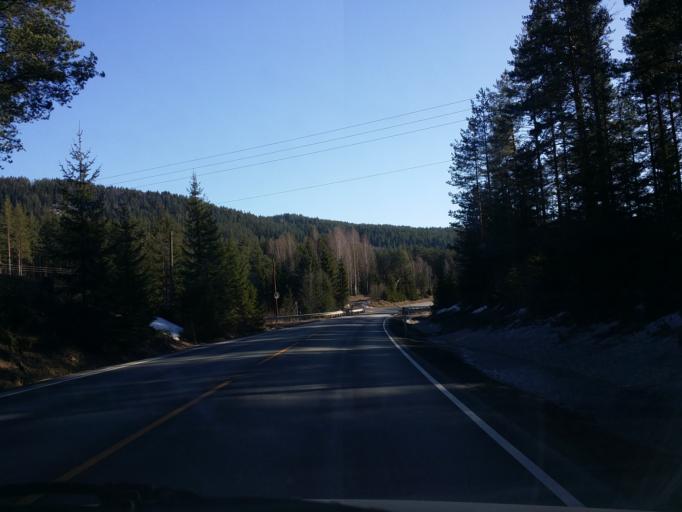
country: NO
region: Buskerud
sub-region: Ringerike
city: Honefoss
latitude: 60.2845
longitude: 10.1943
